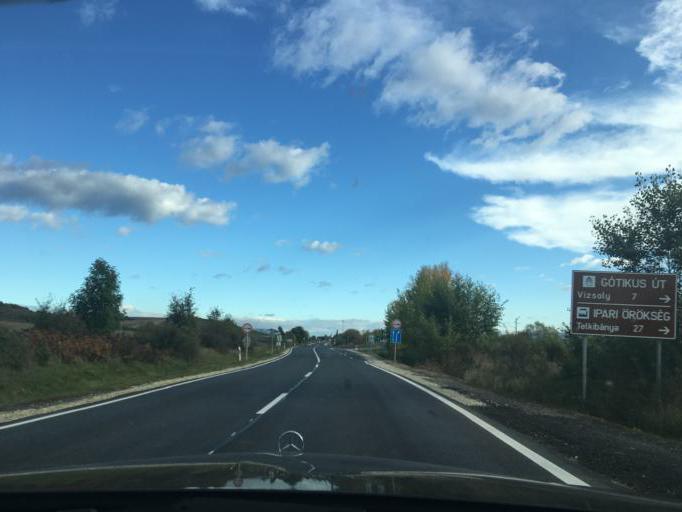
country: HU
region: Borsod-Abauj-Zemplen
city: Encs
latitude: 48.3877
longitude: 21.1552
